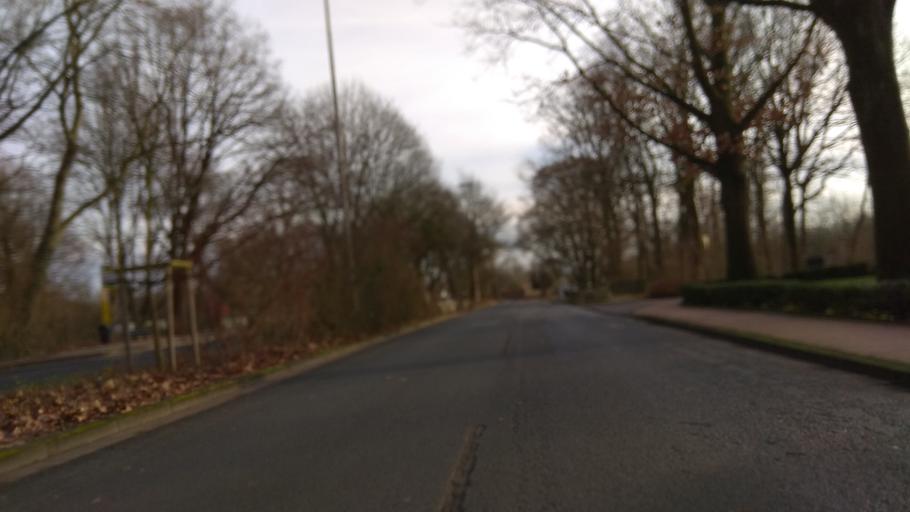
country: DE
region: North Rhine-Westphalia
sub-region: Regierungsbezirk Munster
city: Klein Reken
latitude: 51.7324
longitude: 7.0440
